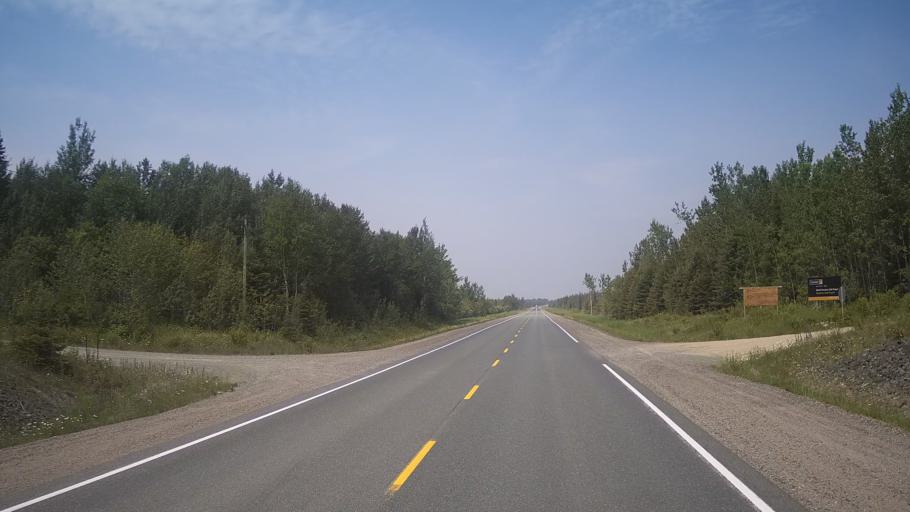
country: CA
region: Ontario
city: Timmins
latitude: 48.7527
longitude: -81.3589
